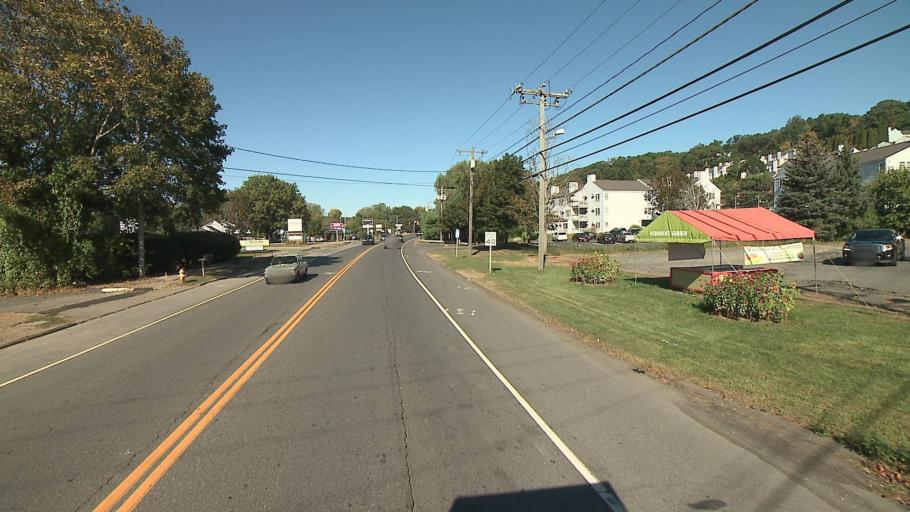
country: US
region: Connecticut
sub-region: Fairfield County
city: Danbury
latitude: 41.3898
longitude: -73.5013
